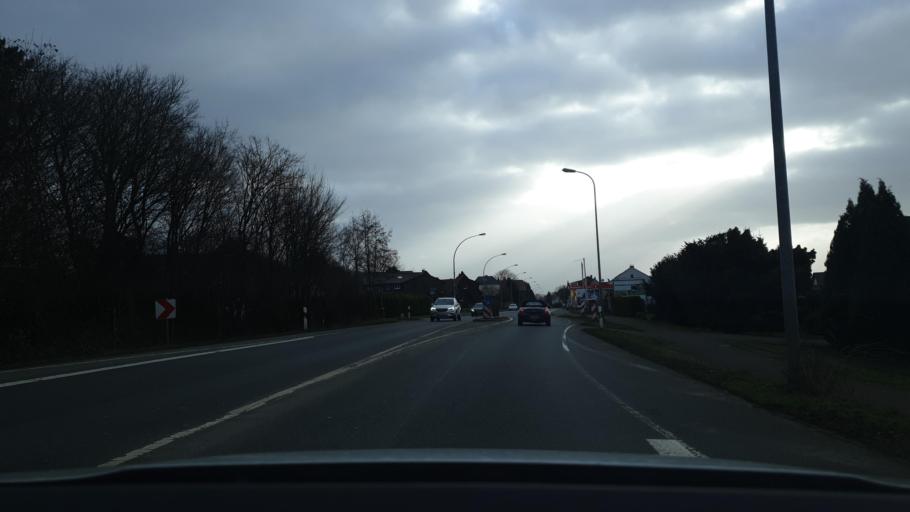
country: DE
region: North Rhine-Westphalia
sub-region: Regierungsbezirk Detmold
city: Huellhorst
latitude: 52.2709
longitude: 8.6357
